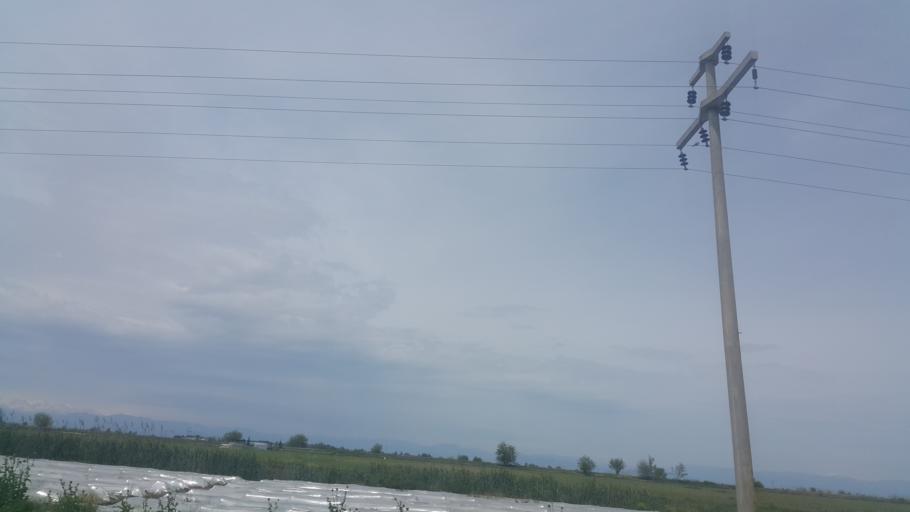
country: TR
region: Adana
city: Ceyhan
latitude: 37.0562
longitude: 35.8751
